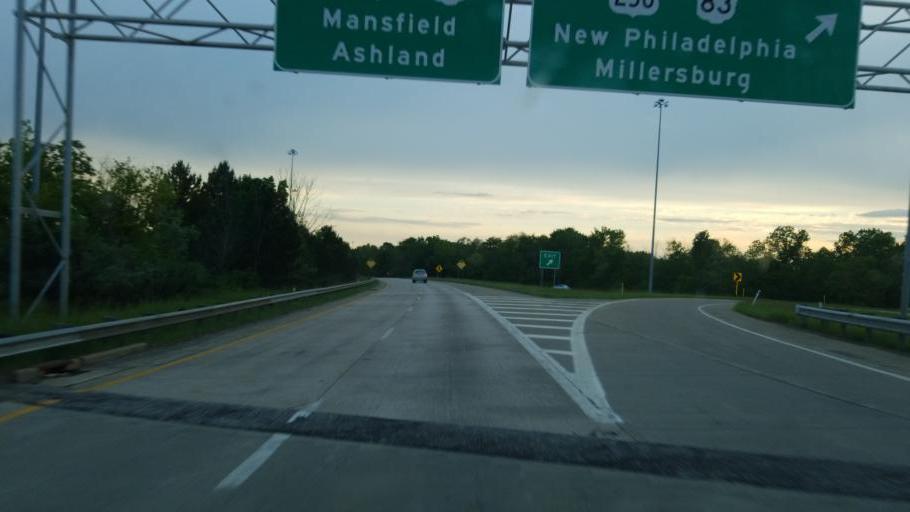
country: US
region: Ohio
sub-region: Wayne County
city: Wooster
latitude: 40.7988
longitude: -81.9128
